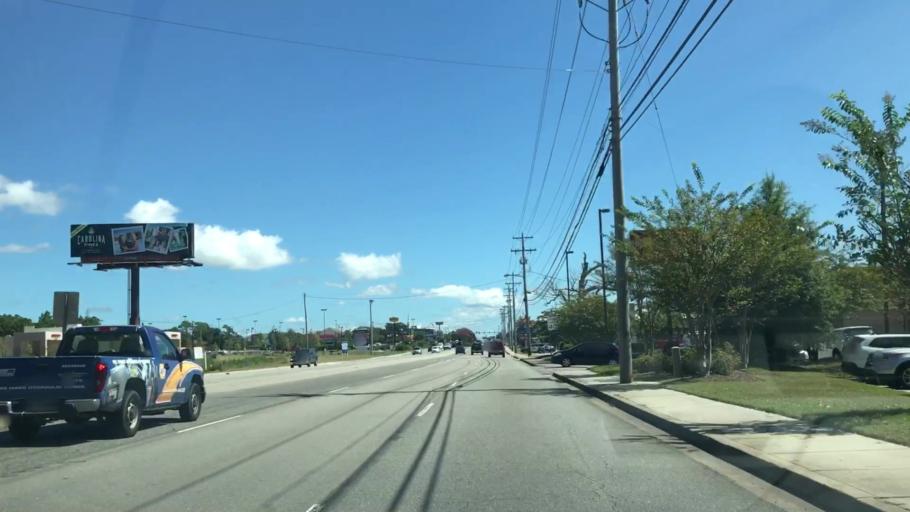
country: US
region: South Carolina
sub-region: Horry County
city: North Myrtle Beach
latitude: 33.8212
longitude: -78.6884
